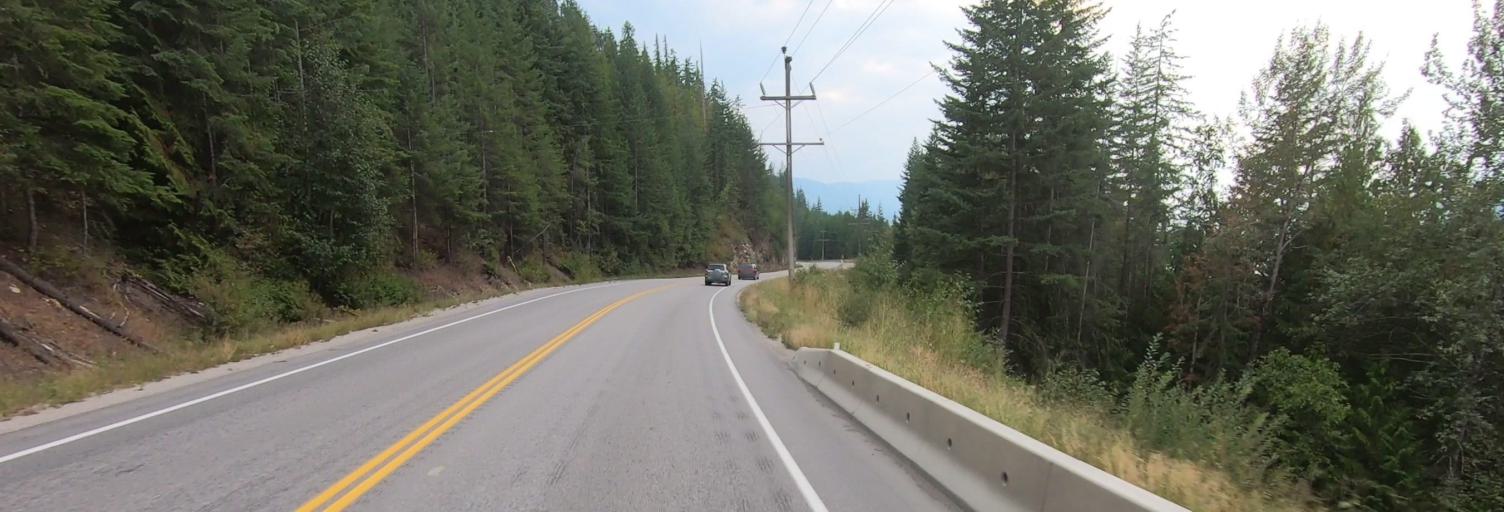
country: CA
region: British Columbia
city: Sicamous
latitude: 50.8219
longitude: -119.0340
